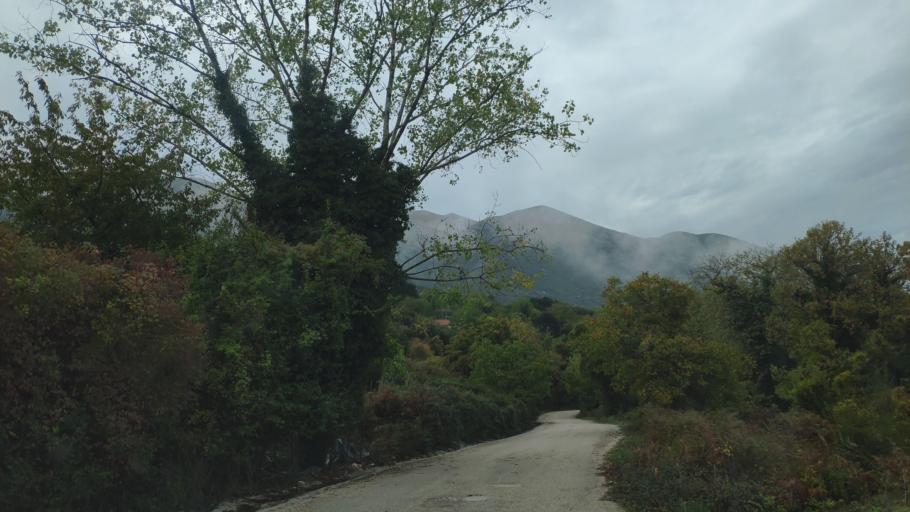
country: GR
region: Epirus
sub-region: Nomos Thesprotias
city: Paramythia
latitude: 39.4598
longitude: 20.6773
